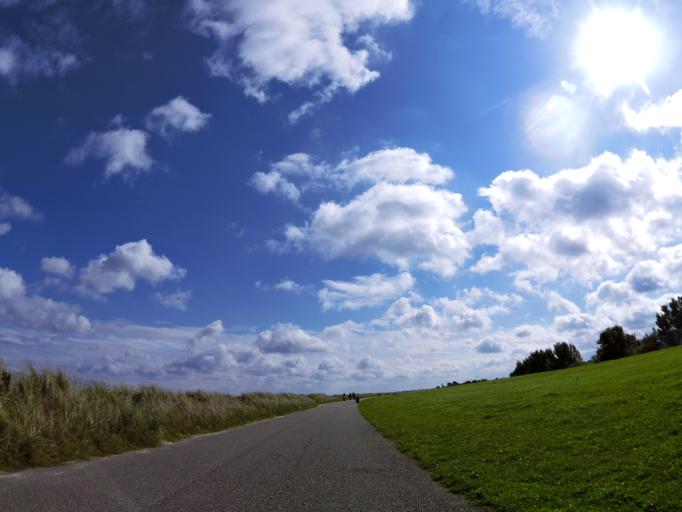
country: DE
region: Schleswig-Holstein
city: Wisch
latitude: 54.4256
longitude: 10.3888
